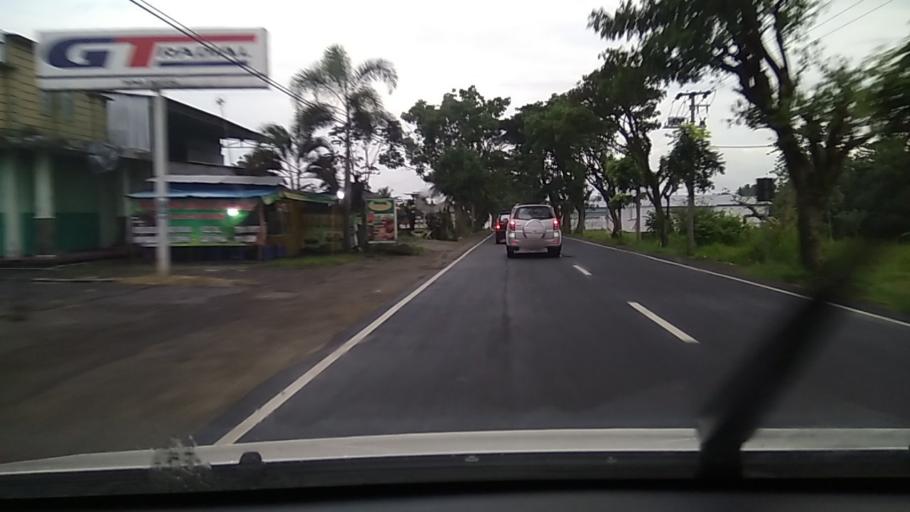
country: ID
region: Bali
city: Pergan
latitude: -8.4383
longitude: 115.1961
